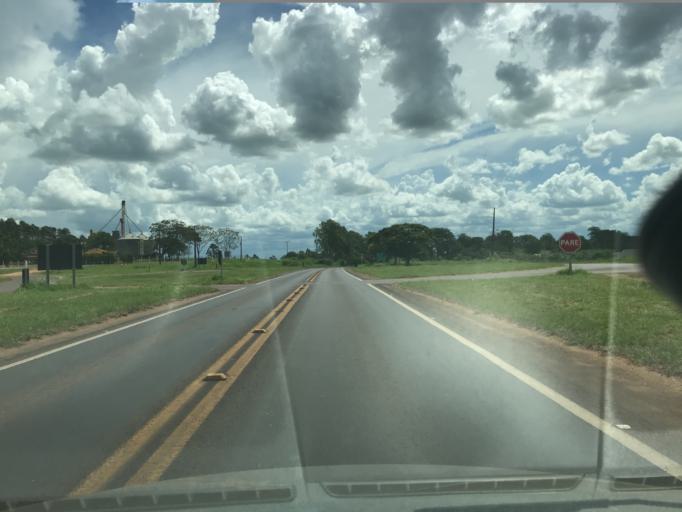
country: BR
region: Parana
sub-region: Cruzeiro Do Oeste
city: Cruzeiro do Oeste
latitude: -23.7986
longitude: -53.0554
